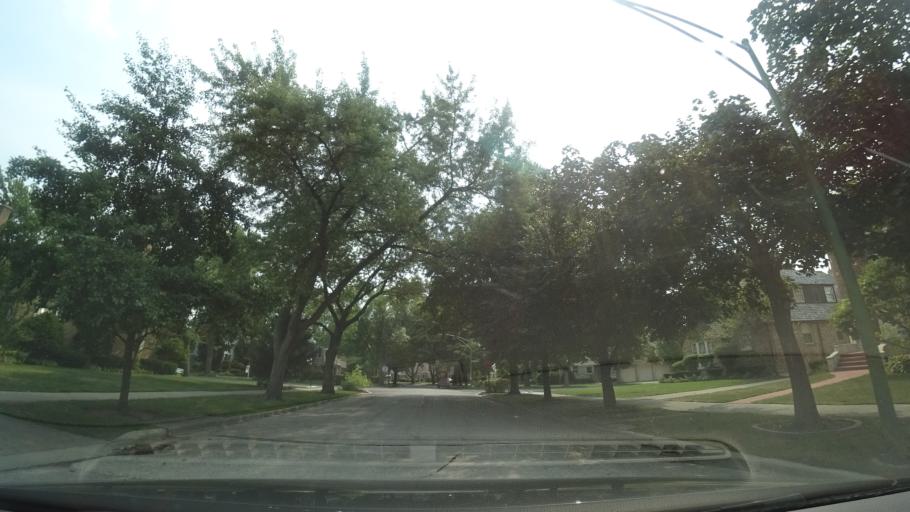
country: US
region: Illinois
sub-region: Cook County
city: Lincolnwood
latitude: 41.9915
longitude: -87.7440
